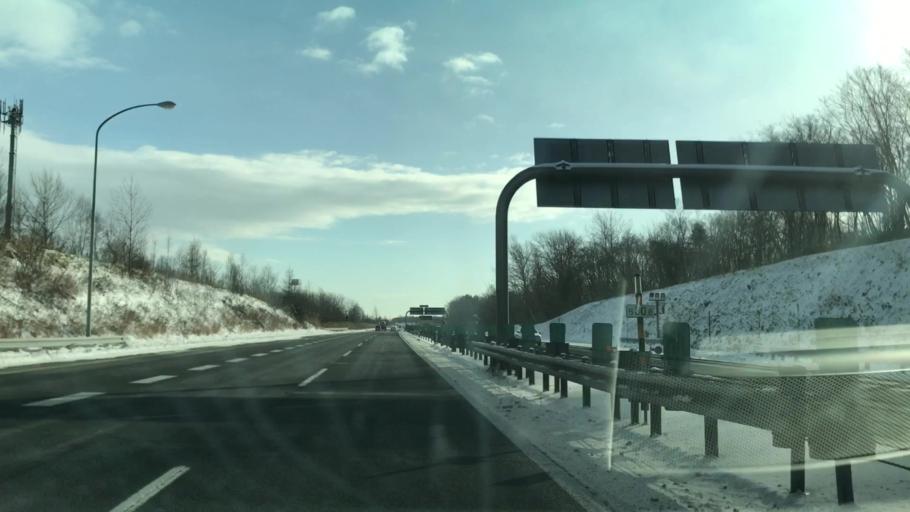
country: JP
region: Hokkaido
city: Chitose
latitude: 42.8435
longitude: 141.5906
